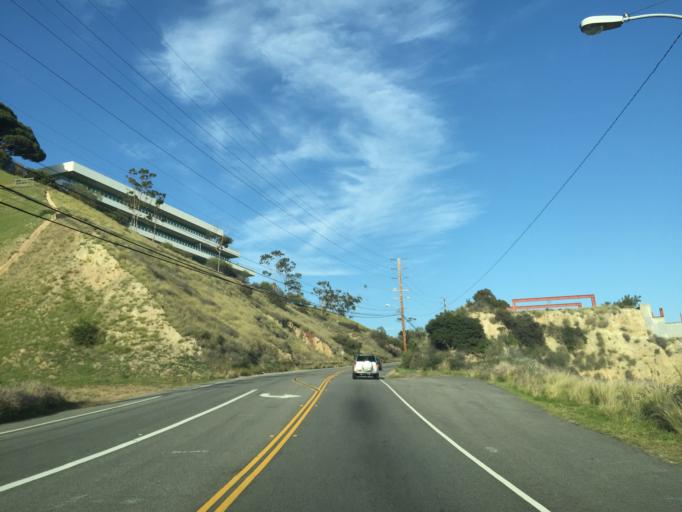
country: US
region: California
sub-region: Los Angeles County
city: Malibu Beach
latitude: 34.0411
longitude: -118.6961
